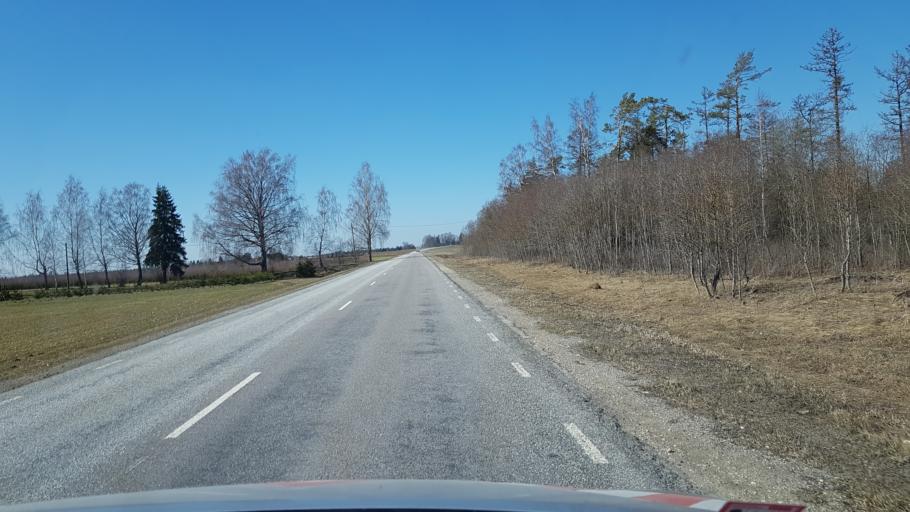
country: EE
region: Laeaene-Virumaa
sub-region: Vaeike-Maarja vald
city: Vaike-Maarja
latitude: 59.1382
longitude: 26.2445
